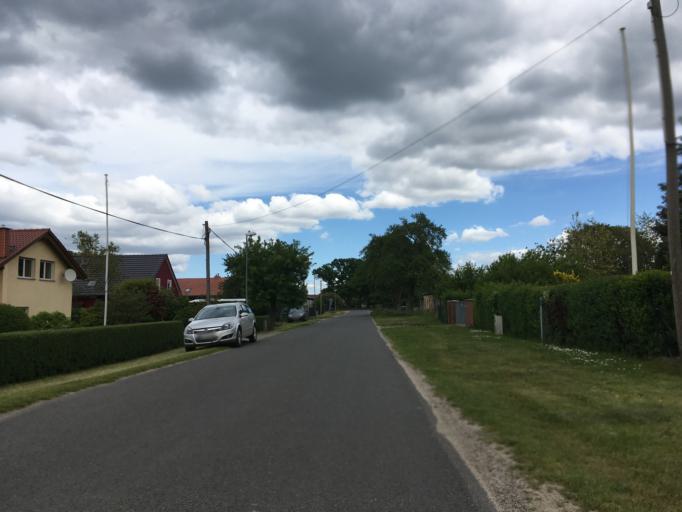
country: DE
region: Brandenburg
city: Hohenfinow
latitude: 52.7697
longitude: 13.9233
